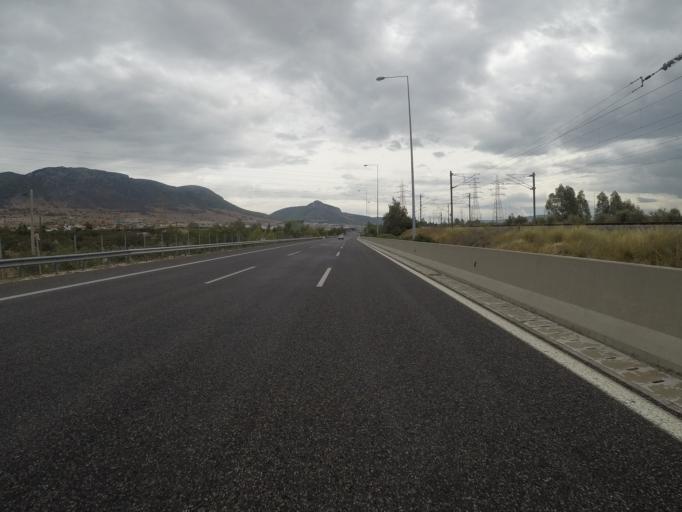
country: GR
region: Attica
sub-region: Nomarchia Dytikis Attikis
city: Aspropyrgos
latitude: 38.0947
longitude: 23.5749
